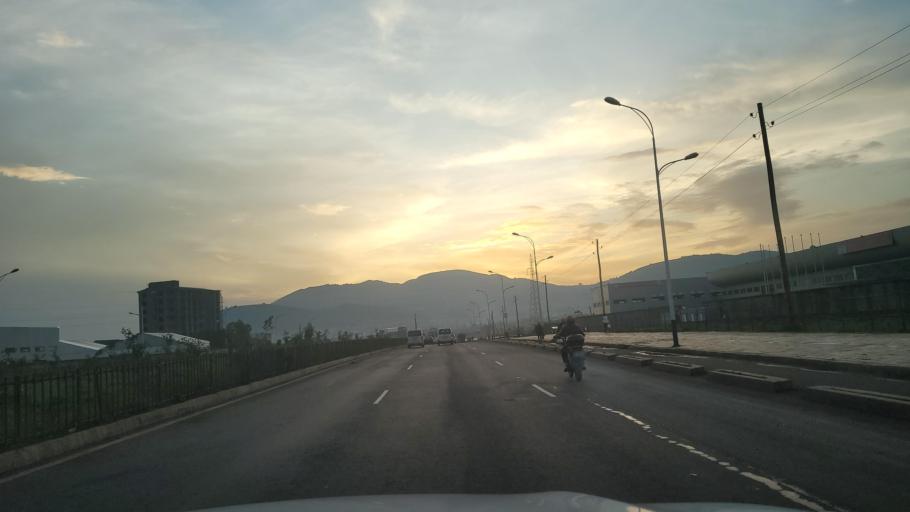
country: ET
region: Adis Abeba
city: Addis Ababa
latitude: 8.9503
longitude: 38.7048
